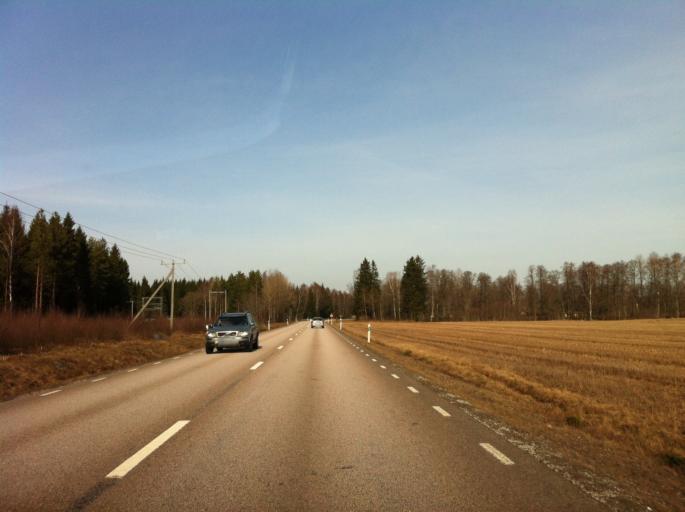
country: SE
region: Vaestra Goetaland
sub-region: Tidaholms Kommun
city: Tidaholm
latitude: 58.0693
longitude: 13.8613
